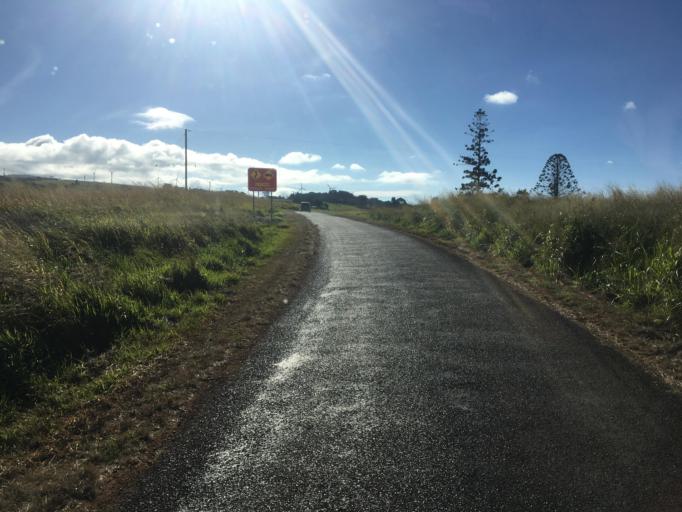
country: AU
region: Queensland
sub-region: Tablelands
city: Ravenshoe
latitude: -17.6052
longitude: 145.5117
